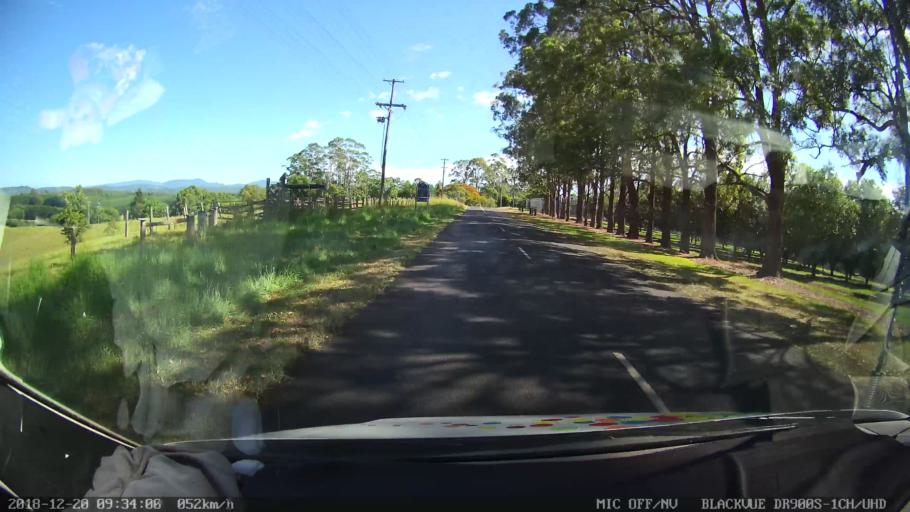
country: AU
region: New South Wales
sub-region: Lismore Municipality
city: Goonellabah
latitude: -28.6931
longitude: 153.3122
